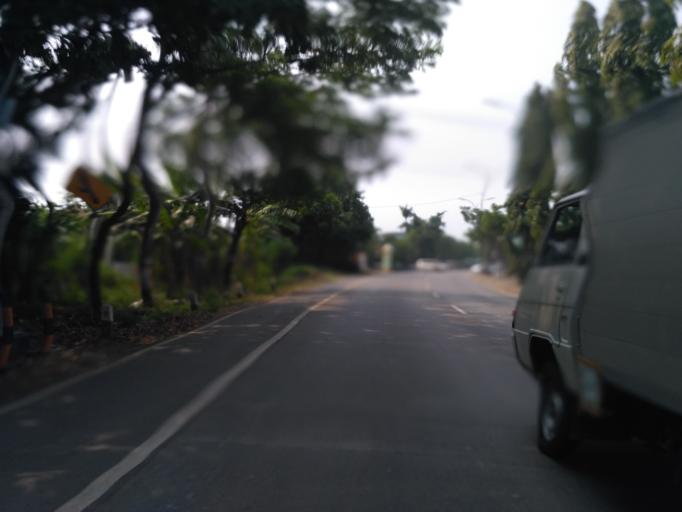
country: ID
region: Central Java
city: Semarang
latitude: -6.9735
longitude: 110.3880
